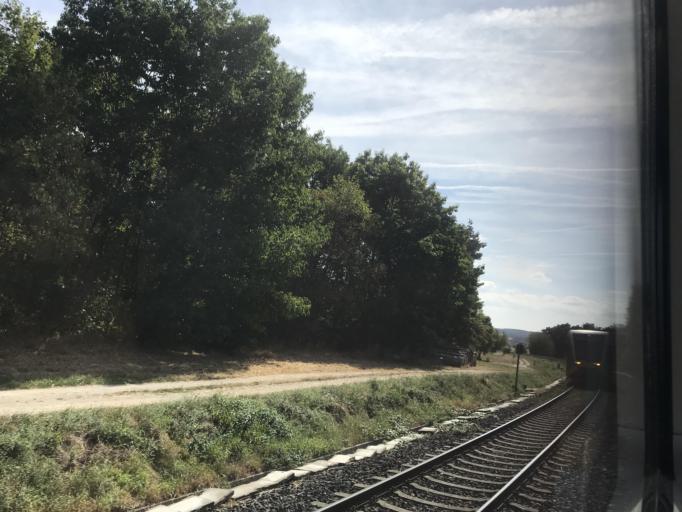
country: DE
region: Hesse
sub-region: Regierungsbezirk Giessen
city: Limburg an der Lahn
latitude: 50.3872
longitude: 8.0395
